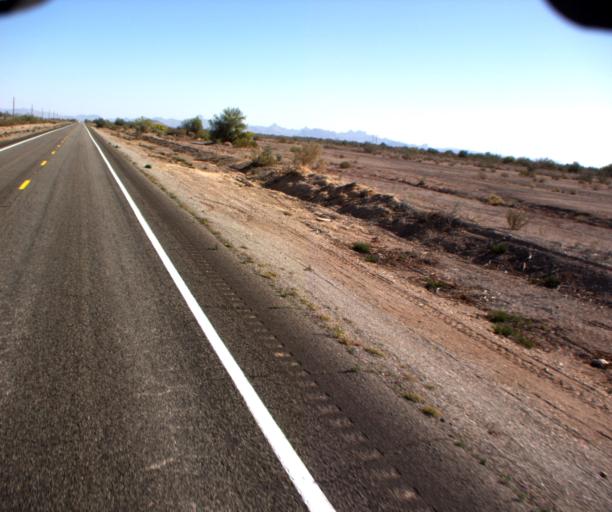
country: US
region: Arizona
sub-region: Yuma County
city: Fortuna Foothills
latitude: 32.8803
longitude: -114.3470
